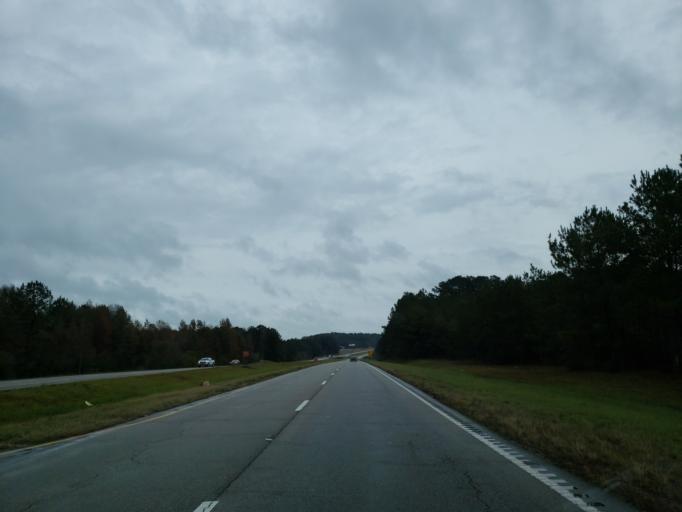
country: US
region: Mississippi
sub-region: Jones County
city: Laurel
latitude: 31.7041
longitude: -89.0785
